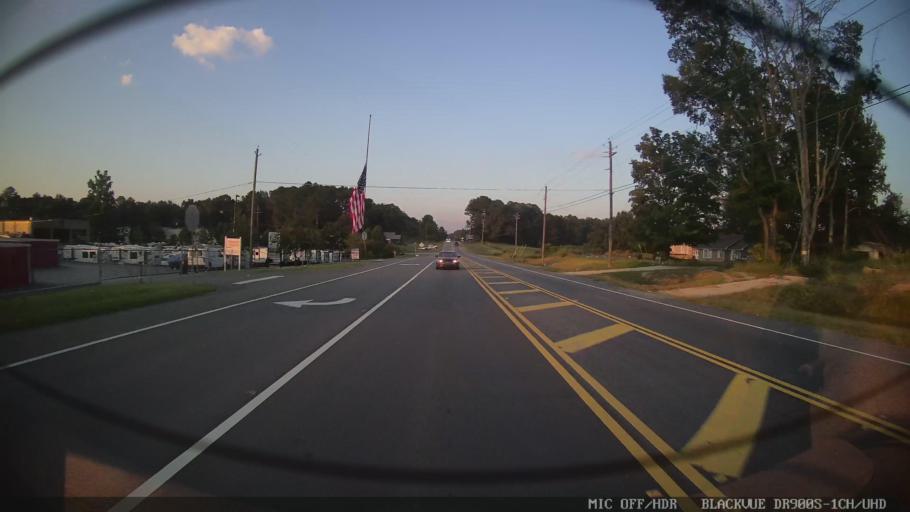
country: US
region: Georgia
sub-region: Bartow County
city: Rydal
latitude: 34.2673
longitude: -84.7553
